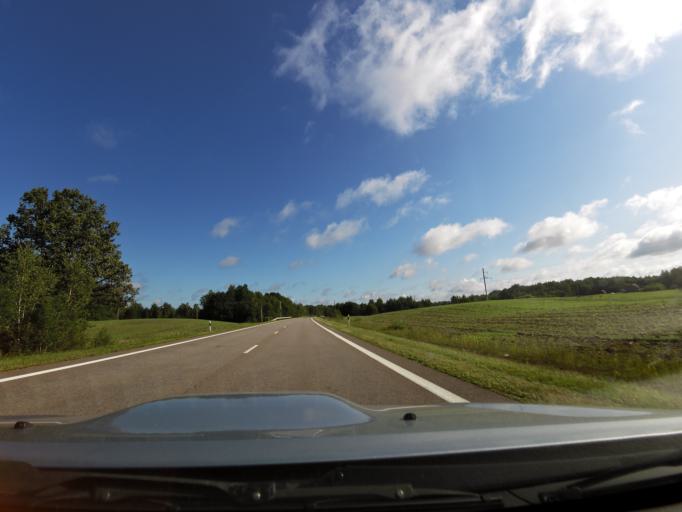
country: LT
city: Moletai
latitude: 55.0953
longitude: 25.3582
